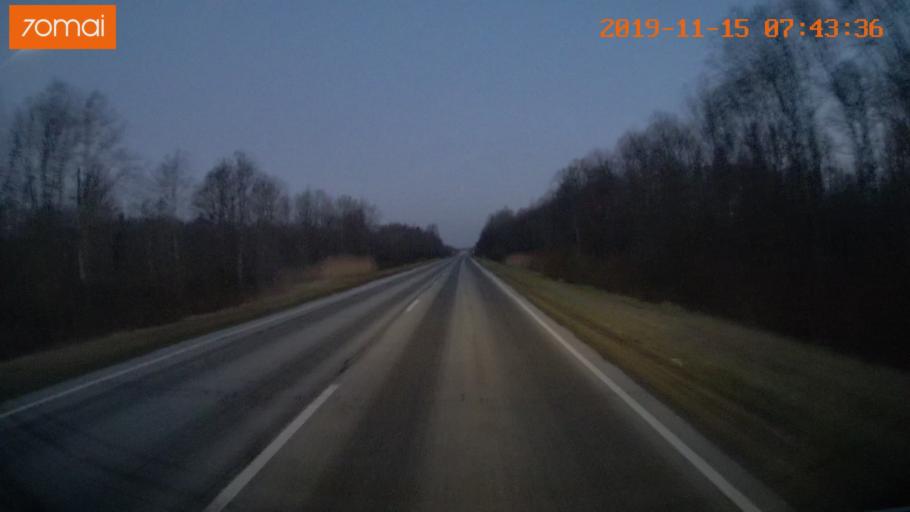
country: RU
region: Vologda
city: Sheksna
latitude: 58.7986
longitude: 38.3328
